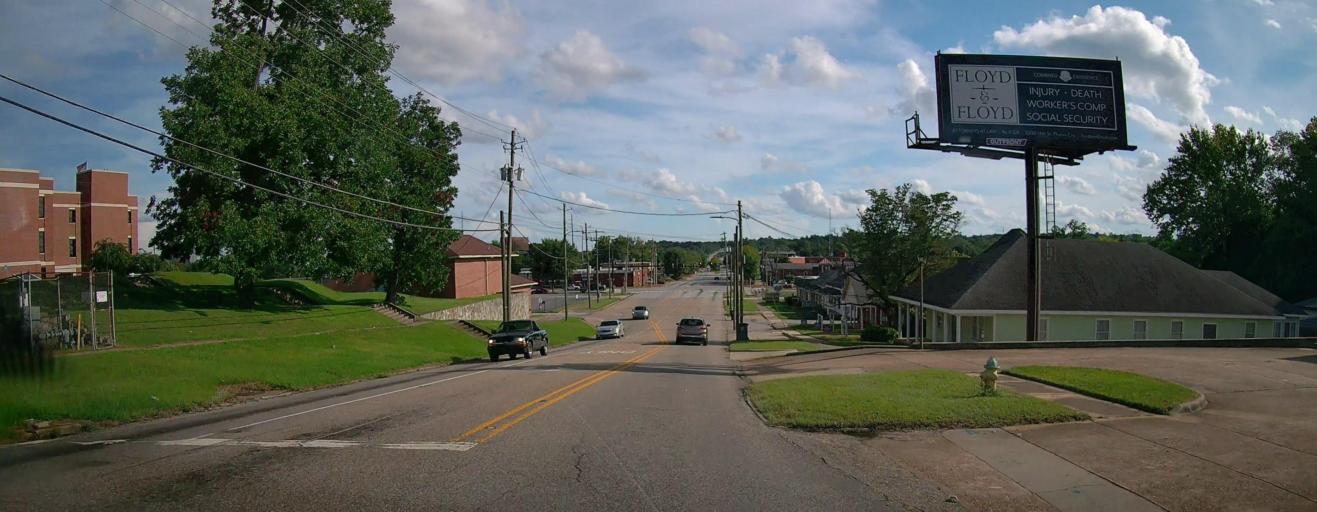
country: US
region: Alabama
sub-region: Russell County
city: Phenix City
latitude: 32.4731
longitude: -85.0008
